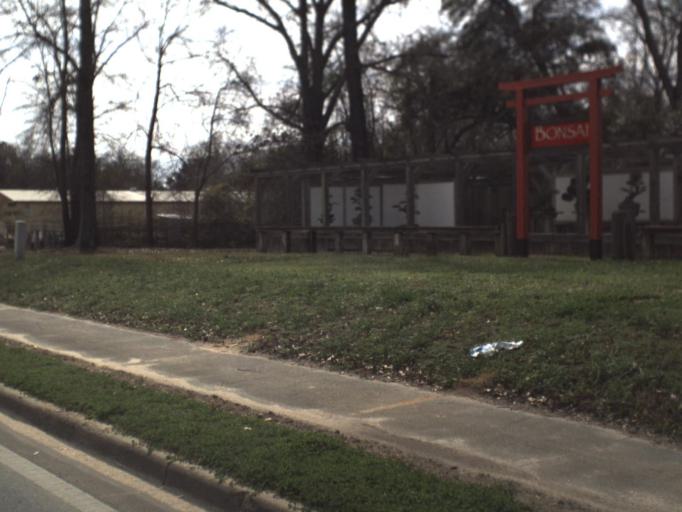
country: US
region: Florida
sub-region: Jackson County
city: Marianna
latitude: 30.7912
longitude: -85.3765
